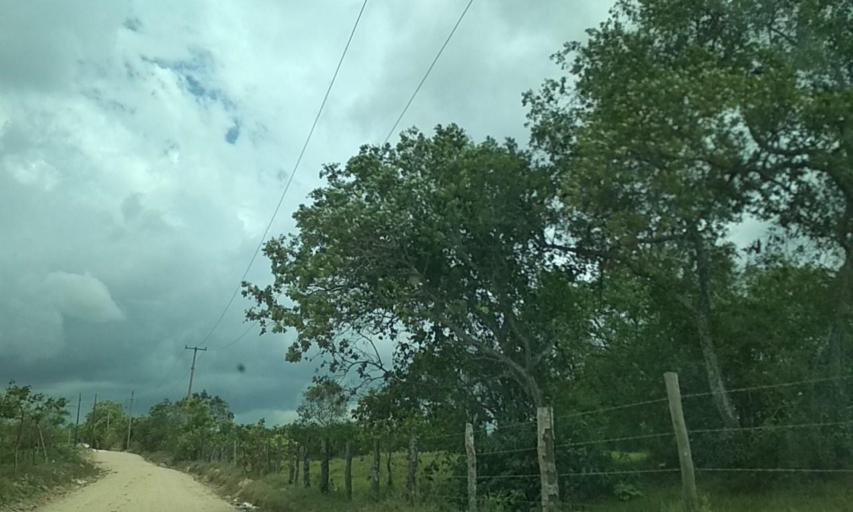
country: MX
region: Veracruz
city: Las Choapas
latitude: 17.9010
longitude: -94.1227
